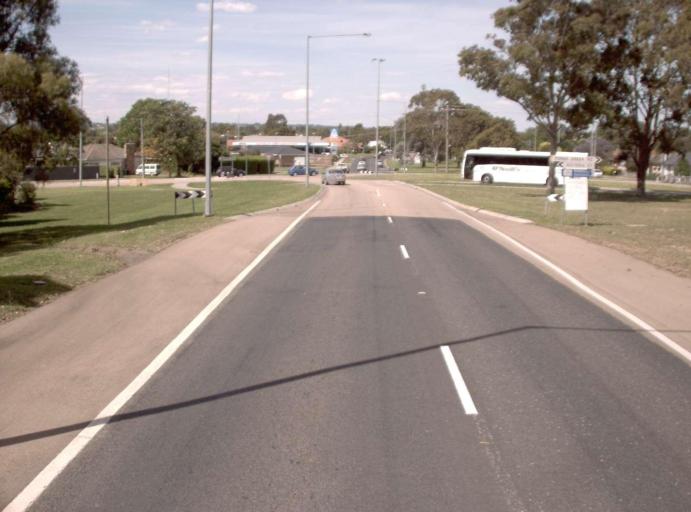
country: AU
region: Victoria
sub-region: East Gippsland
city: Bairnsdale
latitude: -37.8313
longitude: 147.6100
